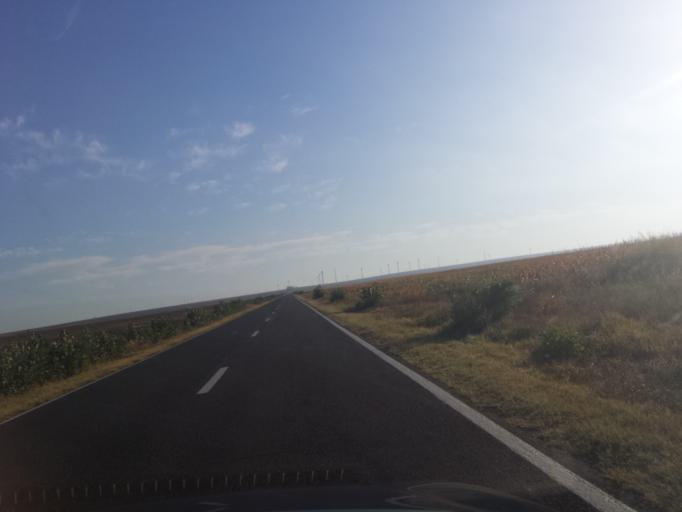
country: RO
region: Constanta
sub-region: Comuna Saraiu
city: Saraiu
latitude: 44.7403
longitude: 28.1757
